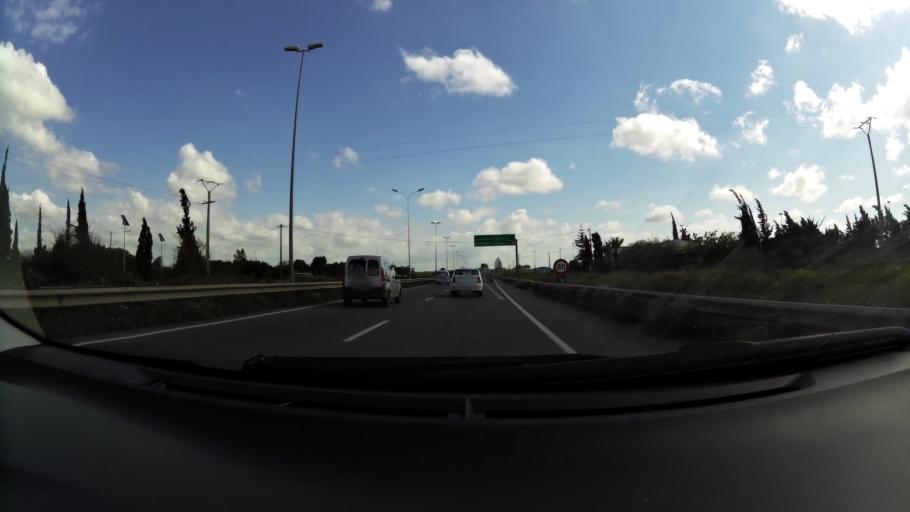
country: MA
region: Chaouia-Ouardigha
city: Nouaseur
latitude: 33.3952
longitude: -7.6202
